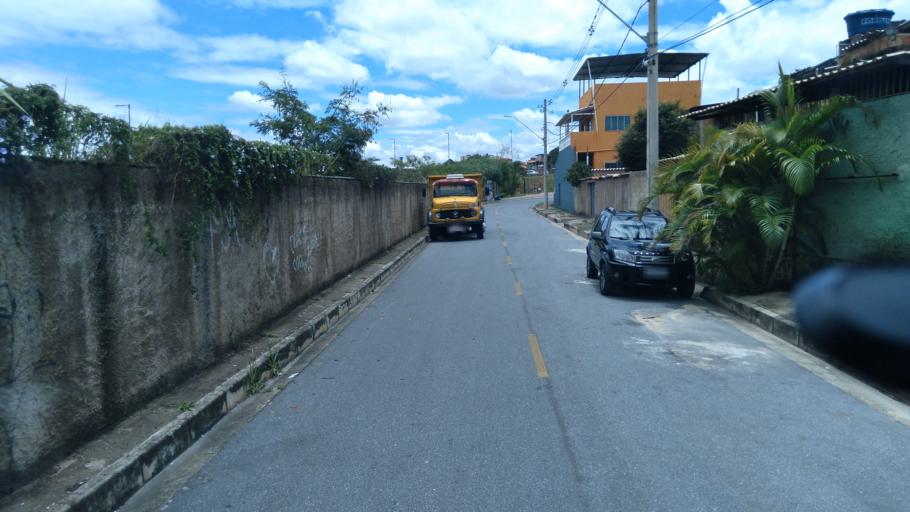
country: BR
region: Minas Gerais
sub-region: Belo Horizonte
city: Belo Horizonte
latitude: -19.9040
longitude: -43.8891
